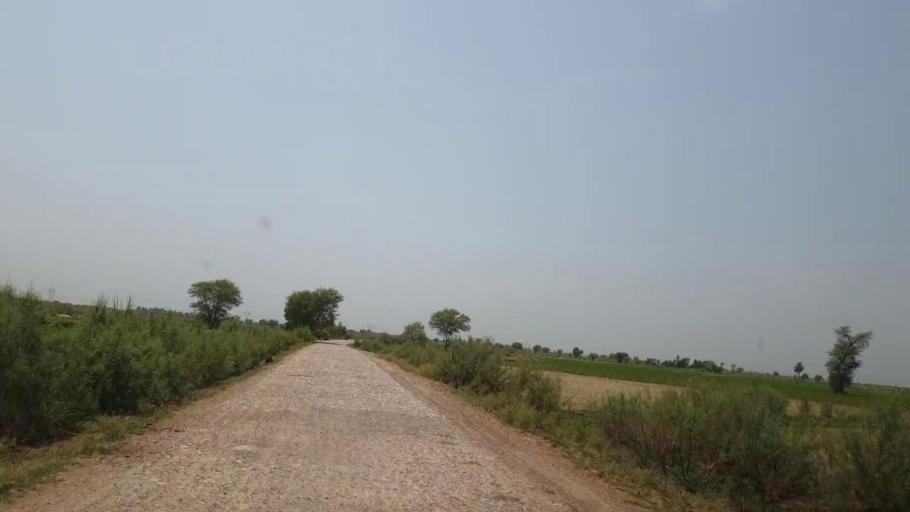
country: PK
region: Sindh
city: Shikarpur
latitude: 27.9034
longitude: 68.6329
